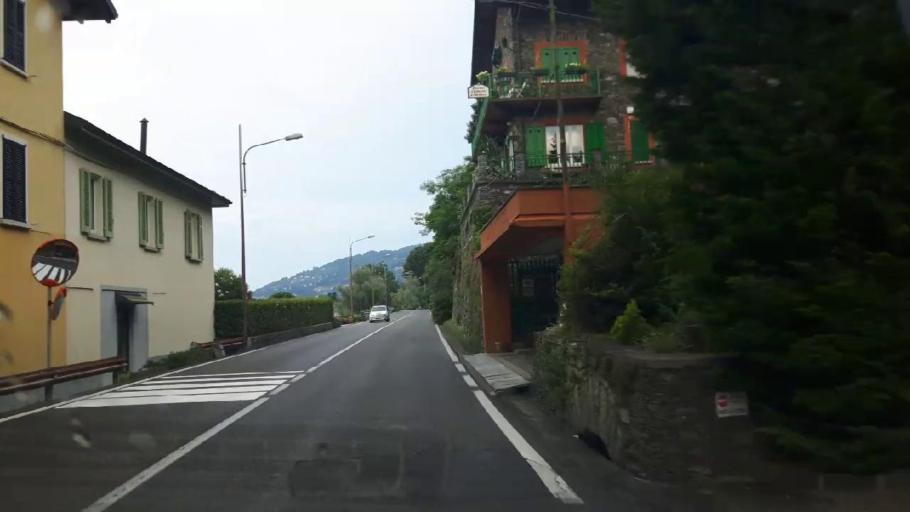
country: IT
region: Piedmont
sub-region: Provincia Verbano-Cusio-Ossola
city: Baveno
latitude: 45.8991
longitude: 8.5114
